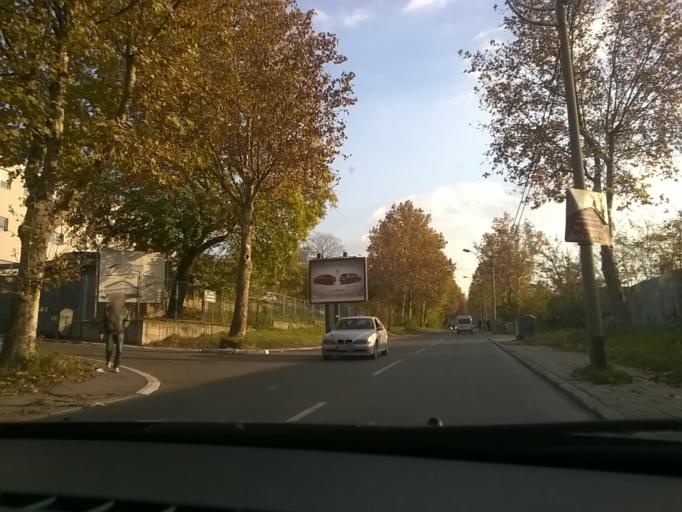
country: RS
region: Central Serbia
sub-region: Belgrade
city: Palilula
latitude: 44.8123
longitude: 20.4926
